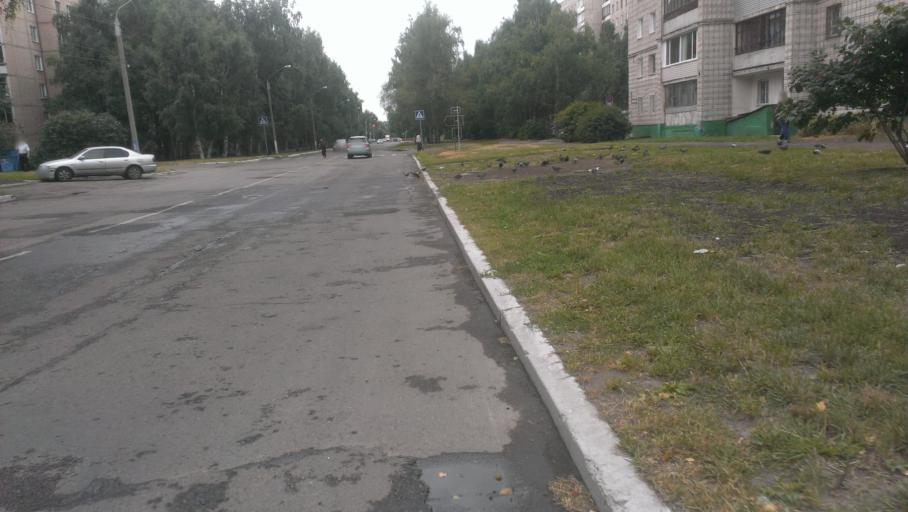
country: RU
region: Altai Krai
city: Novosilikatnyy
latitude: 53.3699
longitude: 83.6692
